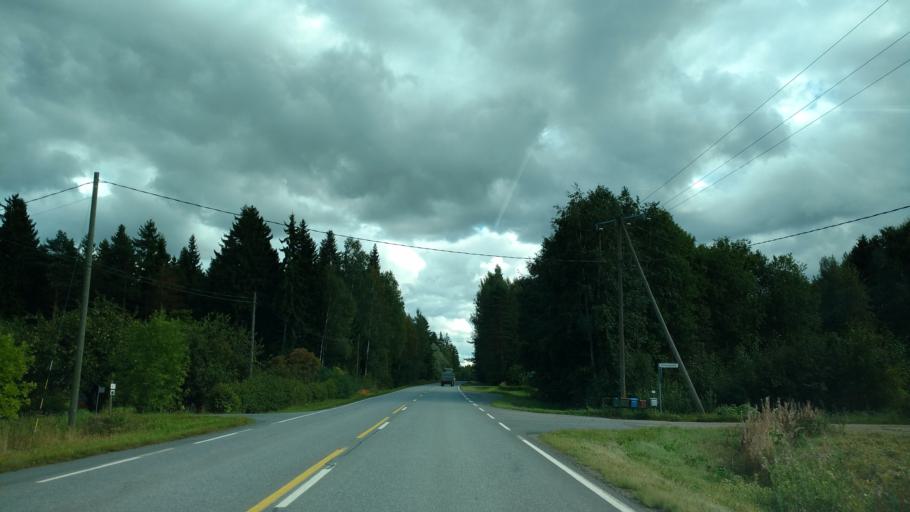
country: FI
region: Haeme
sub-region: Forssa
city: Ypaejae
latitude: 60.8001
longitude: 23.2471
